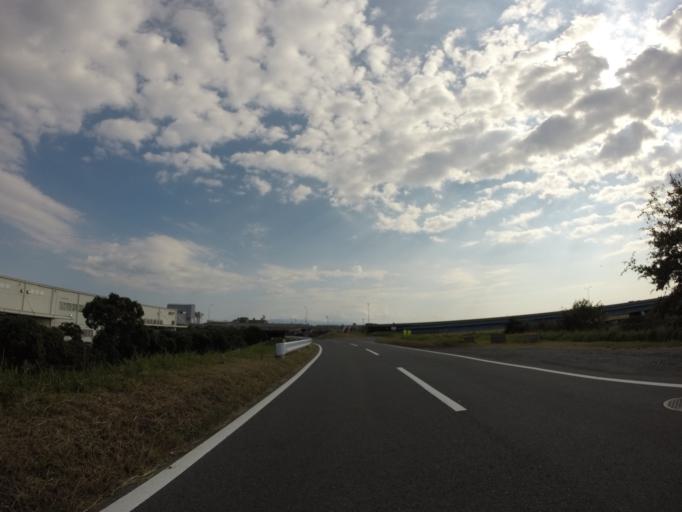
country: JP
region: Shizuoka
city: Fuji
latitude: 35.1326
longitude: 138.6417
